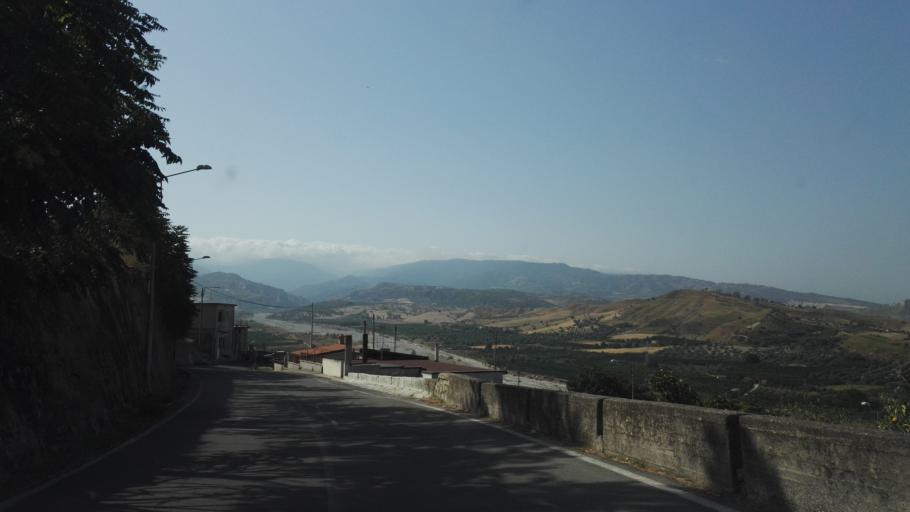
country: IT
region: Calabria
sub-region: Provincia di Reggio Calabria
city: Monasterace
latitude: 38.4543
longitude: 16.5526
